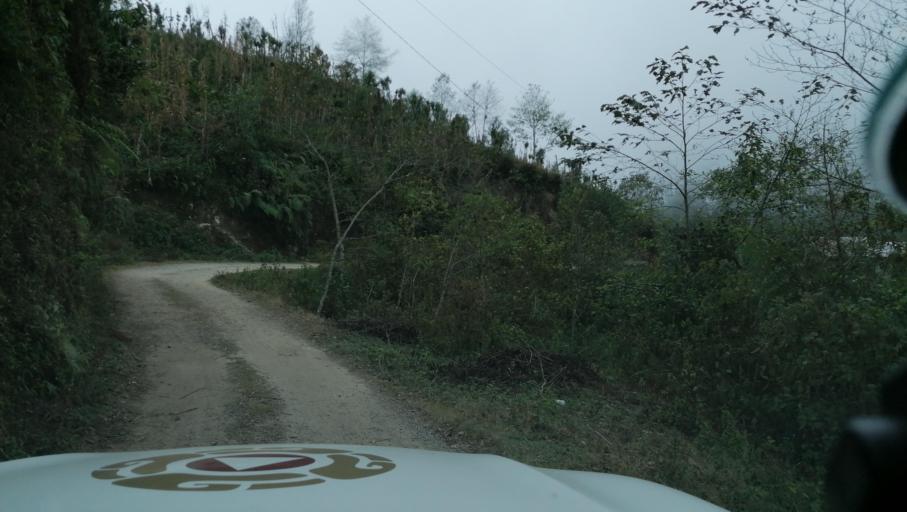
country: MX
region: Chiapas
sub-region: Cacahoatan
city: Benito Juarez
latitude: 15.1967
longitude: -92.2290
